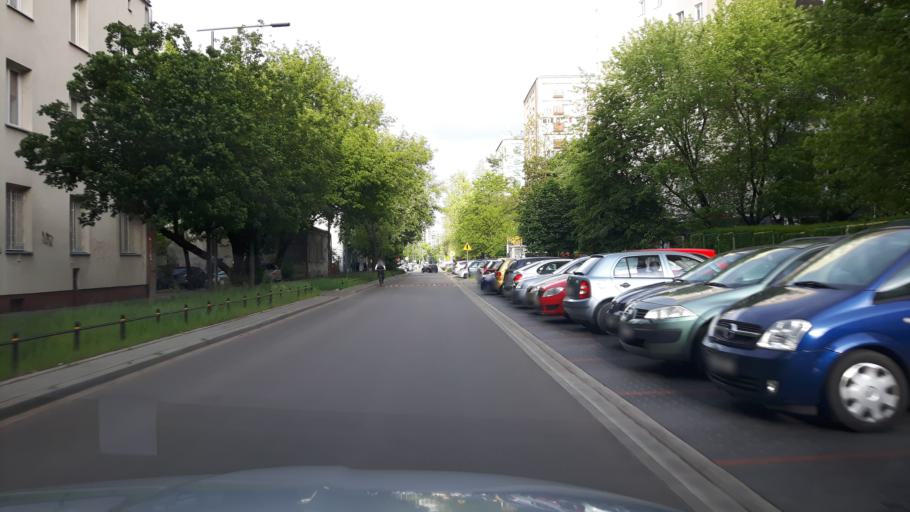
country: PL
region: Masovian Voivodeship
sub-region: Warszawa
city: Praga Poludnie
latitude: 52.2471
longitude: 21.0869
